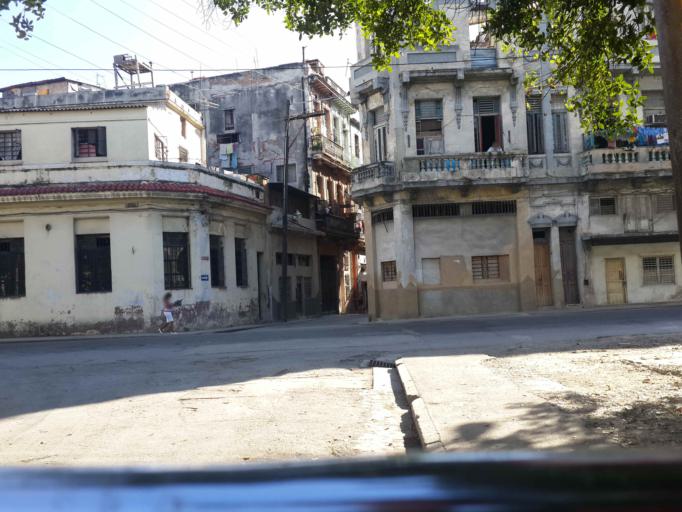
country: CU
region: La Habana
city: La Habana Vieja
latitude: 23.1314
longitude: -82.3551
